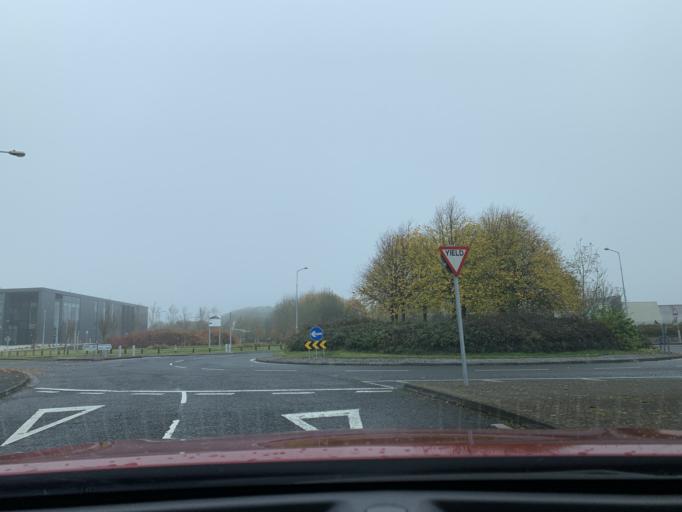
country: IE
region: Connaught
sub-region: Sligo
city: Sligo
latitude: 54.2767
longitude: -8.5027
